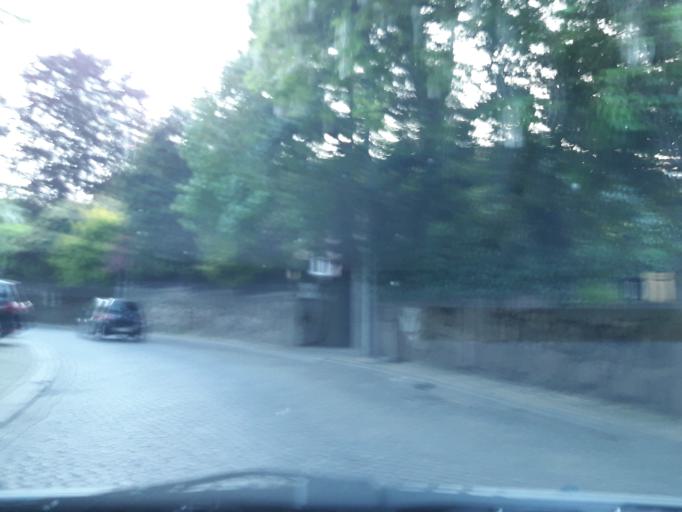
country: PT
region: Braga
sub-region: Vila Nova de Famalicao
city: Vila Nova de Famalicao
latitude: 41.4076
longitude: -8.5247
